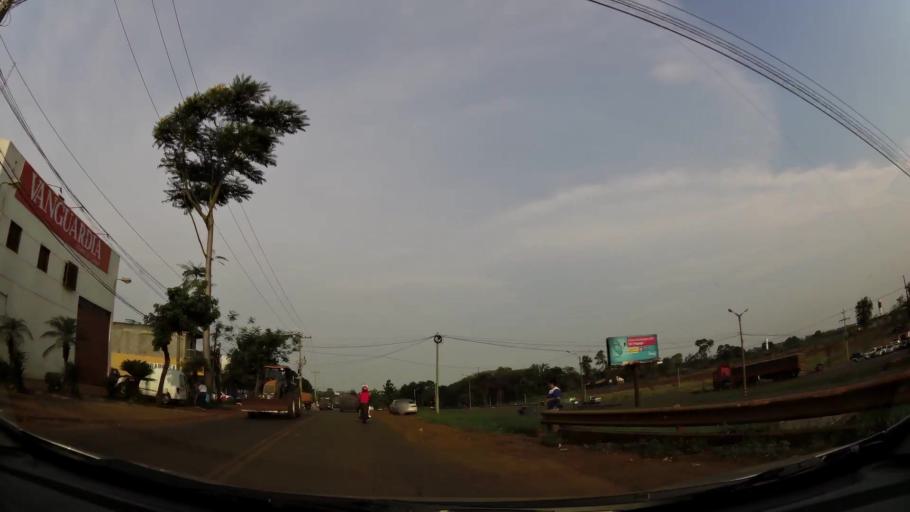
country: PY
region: Alto Parana
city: Ciudad del Este
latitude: -25.4961
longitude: -54.6778
